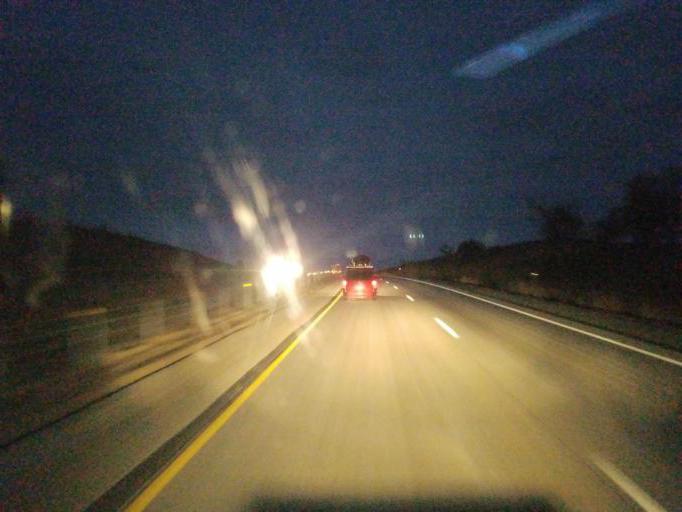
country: US
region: Iowa
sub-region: Guthrie County
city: Guthrie Center
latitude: 41.4931
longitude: -94.6011
